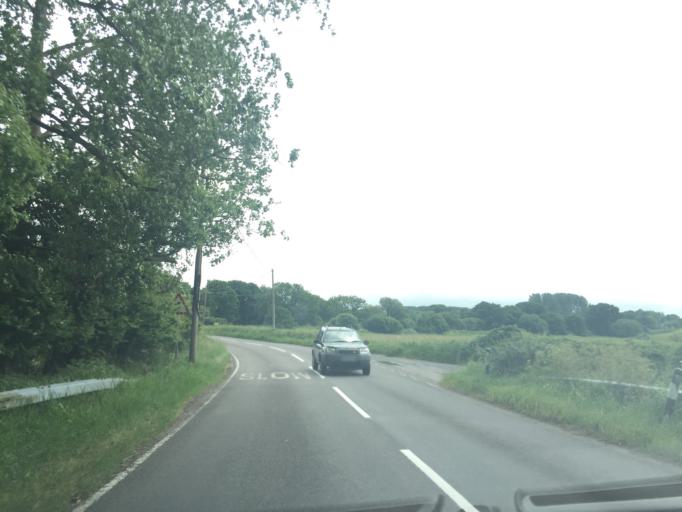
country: GB
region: England
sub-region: Dorset
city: Wareham
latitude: 50.6792
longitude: -2.1561
